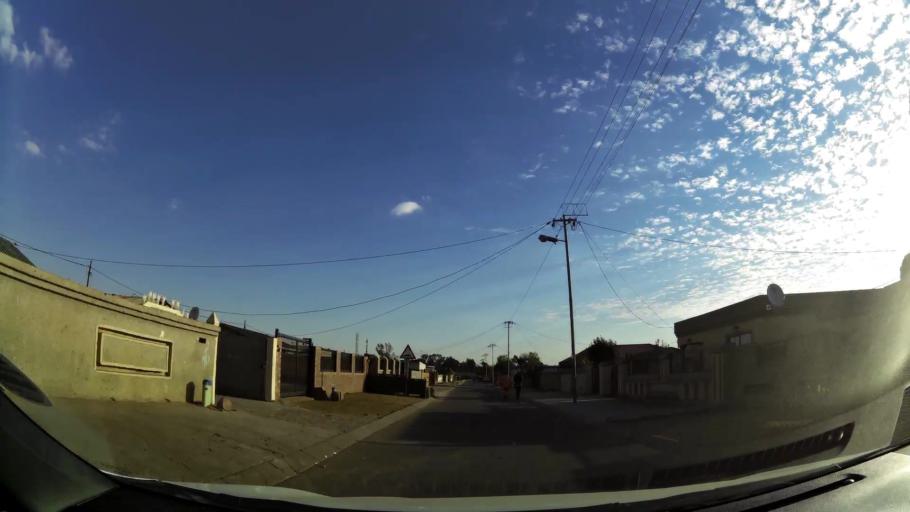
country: ZA
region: Gauteng
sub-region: City of Tshwane Metropolitan Municipality
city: Cullinan
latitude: -25.7087
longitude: 28.3810
